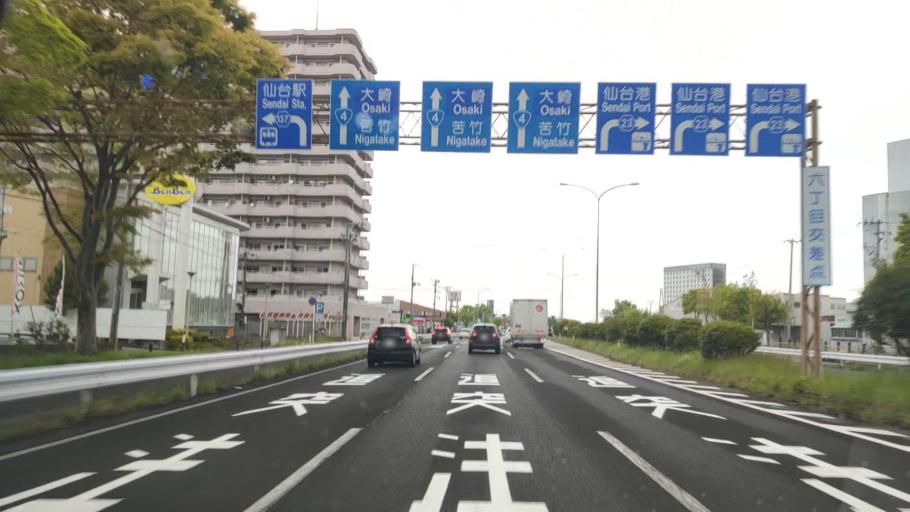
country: JP
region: Miyagi
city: Sendai-shi
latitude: 38.2487
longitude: 140.9259
